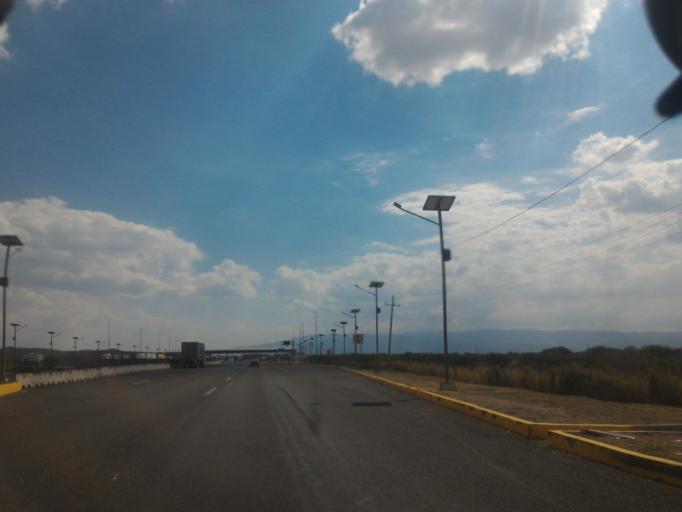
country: MX
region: Jalisco
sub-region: Acatlan de Juarez
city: Villa de los Ninos
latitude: 20.3770
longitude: -103.5764
